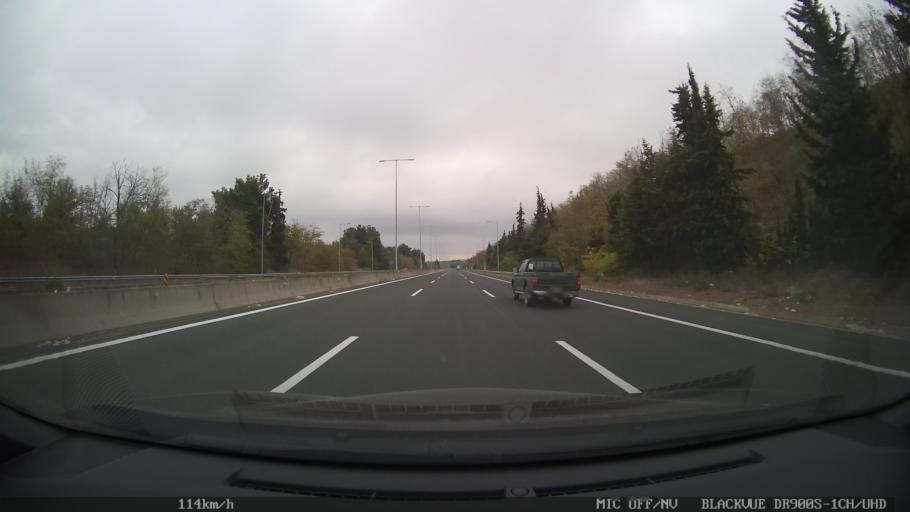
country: GR
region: Central Macedonia
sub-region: Nomos Pierias
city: Makrygialos
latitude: 40.4262
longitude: 22.5892
